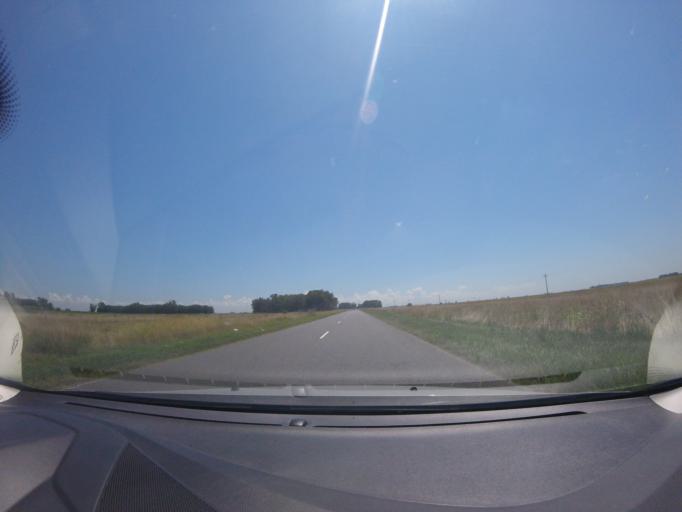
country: AR
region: Buenos Aires
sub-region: Partido de Rauch
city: Rauch
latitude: -36.4639
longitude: -59.0194
